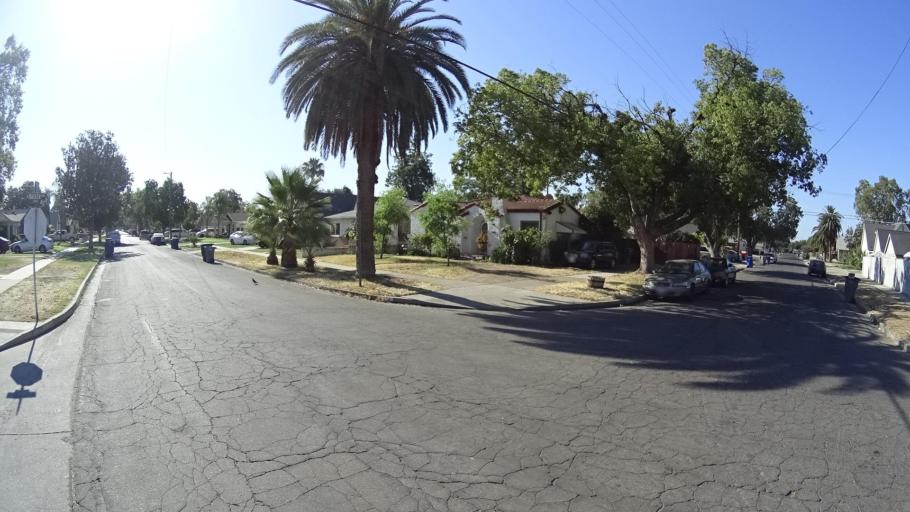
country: US
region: California
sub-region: Fresno County
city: Fresno
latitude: 36.7460
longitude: -119.7432
